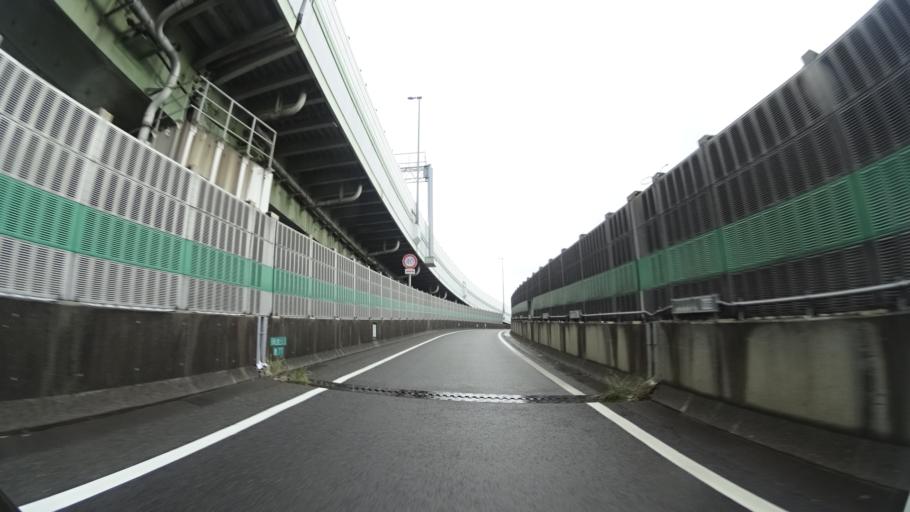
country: JP
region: Hyogo
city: Amagasaki
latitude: 34.6565
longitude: 135.4392
